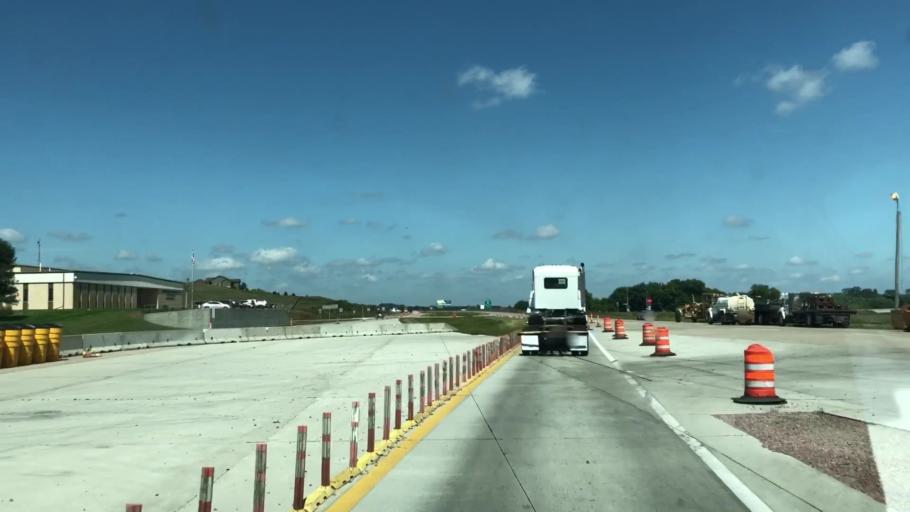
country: US
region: Iowa
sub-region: Plymouth County
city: Le Mars
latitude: 42.7477
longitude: -96.2124
